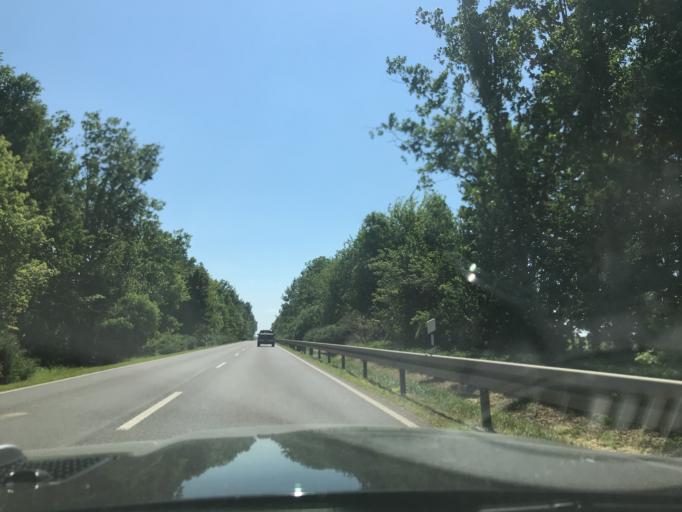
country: DE
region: Thuringia
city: Westhausen
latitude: 51.0274
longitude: 10.6759
